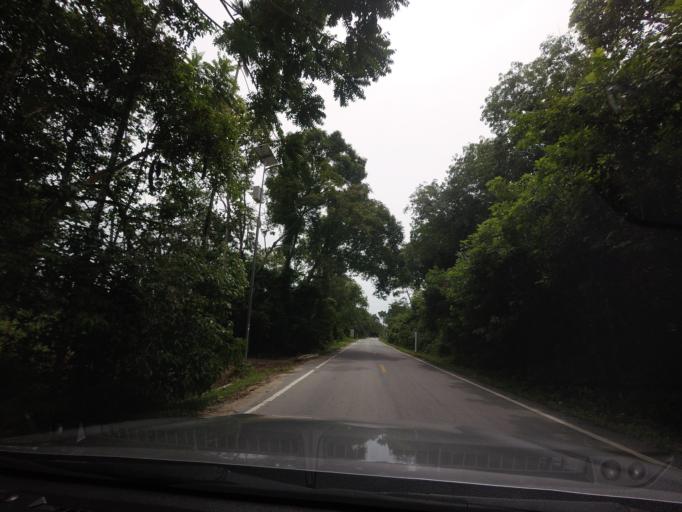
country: TH
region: Pattani
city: Kapho
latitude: 6.6040
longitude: 101.5337
